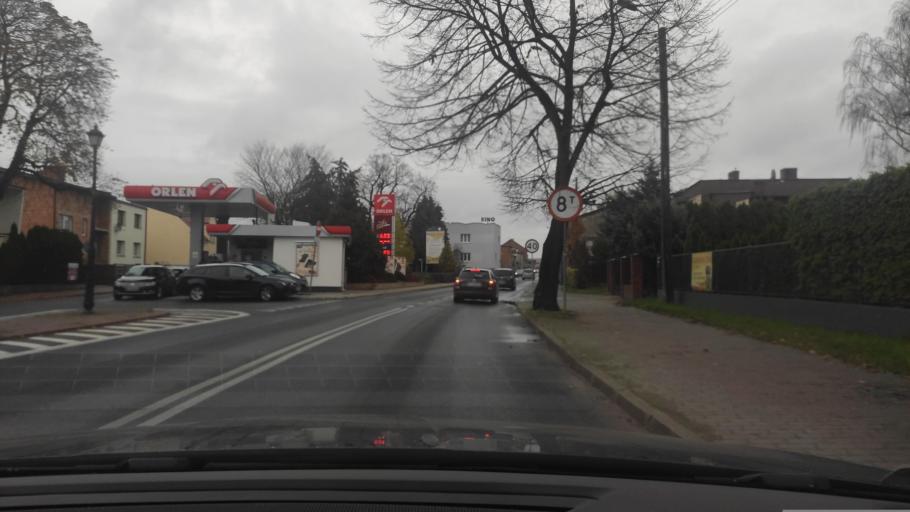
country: PL
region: Greater Poland Voivodeship
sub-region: Powiat poznanski
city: Kostrzyn
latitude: 52.3982
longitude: 17.2219
